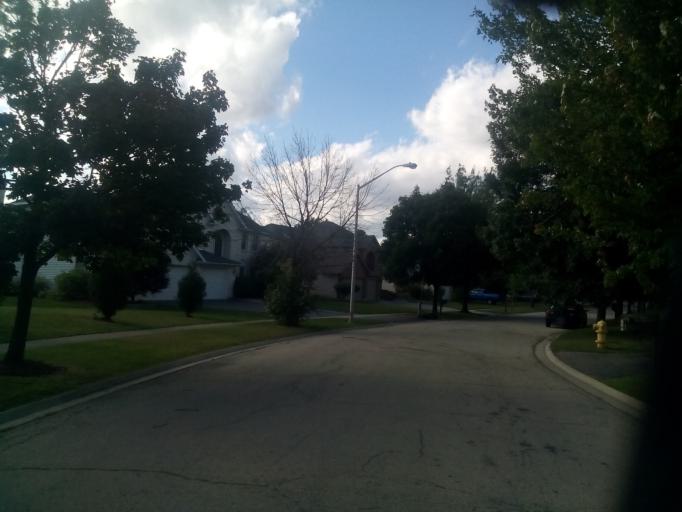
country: US
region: Illinois
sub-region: Will County
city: Romeoville
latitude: 41.6964
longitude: -88.1513
